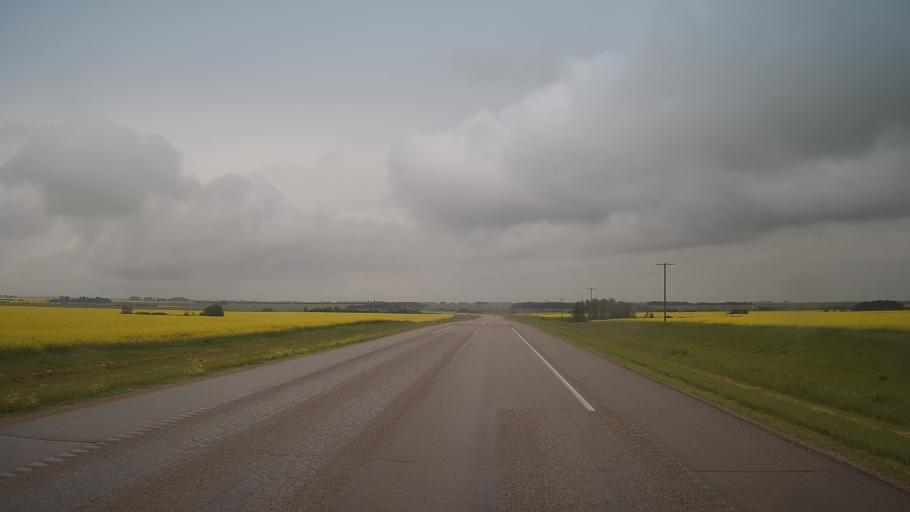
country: CA
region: Saskatchewan
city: Wilkie
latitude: 52.4304
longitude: -108.9190
